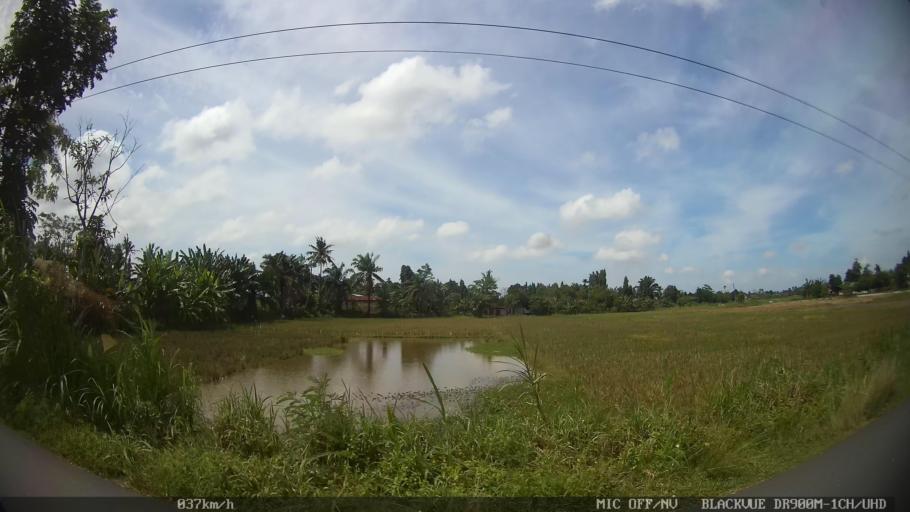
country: ID
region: North Sumatra
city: Percut
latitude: 3.5892
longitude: 98.8704
